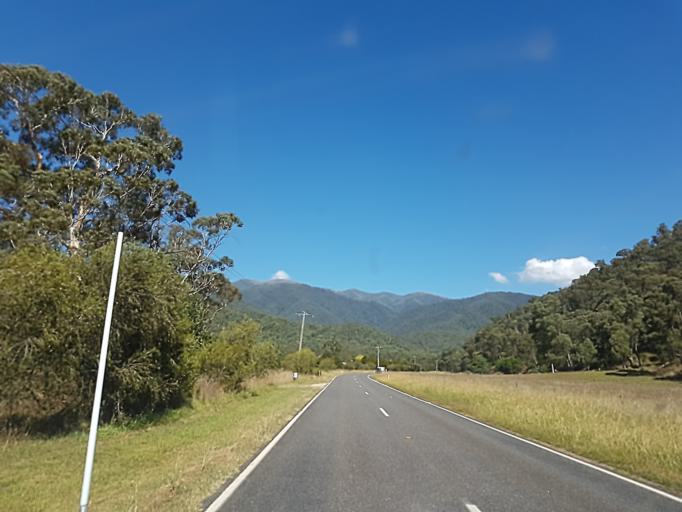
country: AU
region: Victoria
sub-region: Alpine
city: Mount Beauty
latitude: -36.8351
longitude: 147.0758
